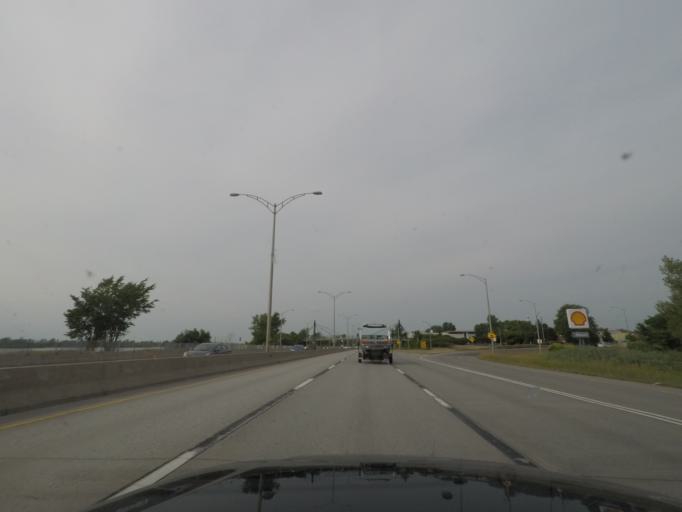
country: CA
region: Quebec
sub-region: Monteregie
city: La Prairie
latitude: 45.4166
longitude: -73.4999
